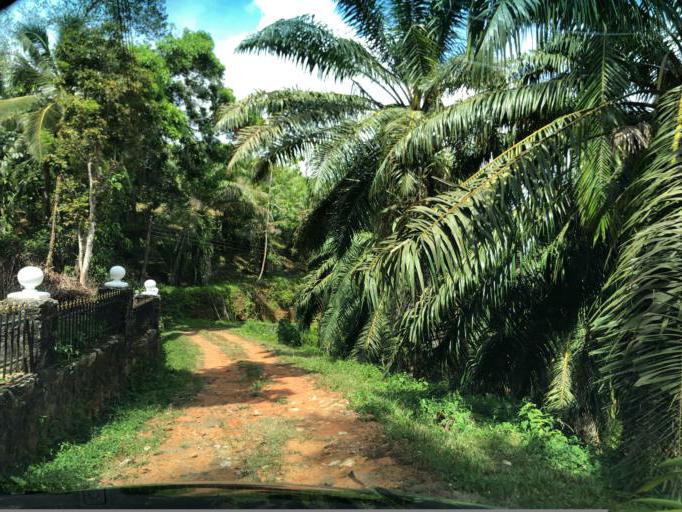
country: LK
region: Western
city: Horawala Junction
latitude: 6.5492
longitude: 80.0882
